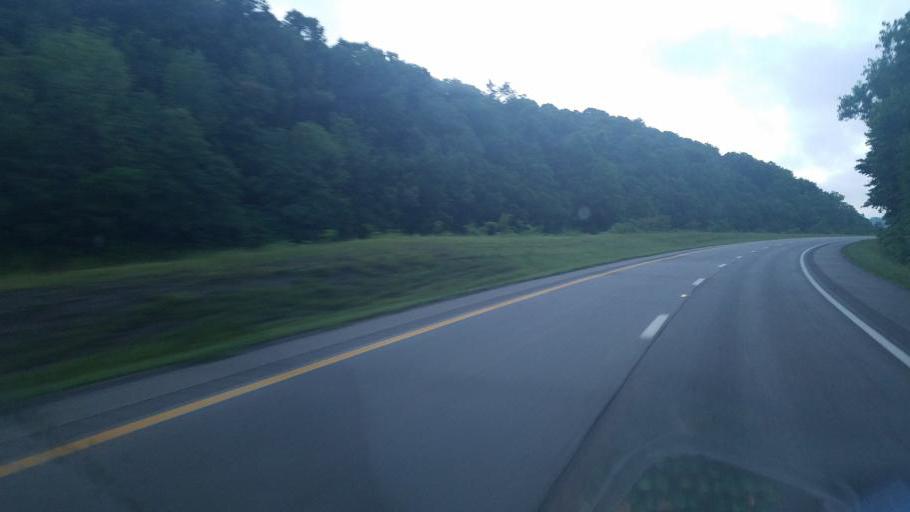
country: US
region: Ohio
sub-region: Pike County
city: Waverly
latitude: 39.1959
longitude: -82.7888
